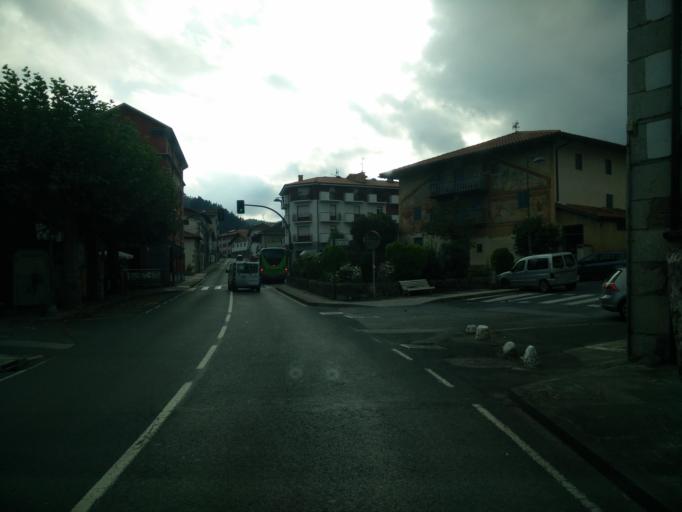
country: ES
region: Basque Country
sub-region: Bizkaia
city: Berriatua
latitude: 43.3094
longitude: -2.4683
